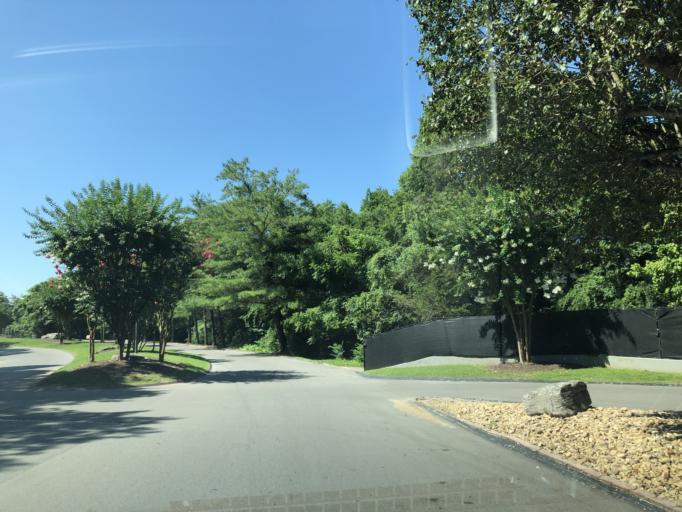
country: US
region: Tennessee
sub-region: Williamson County
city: Nolensville
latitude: 36.0426
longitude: -86.6695
